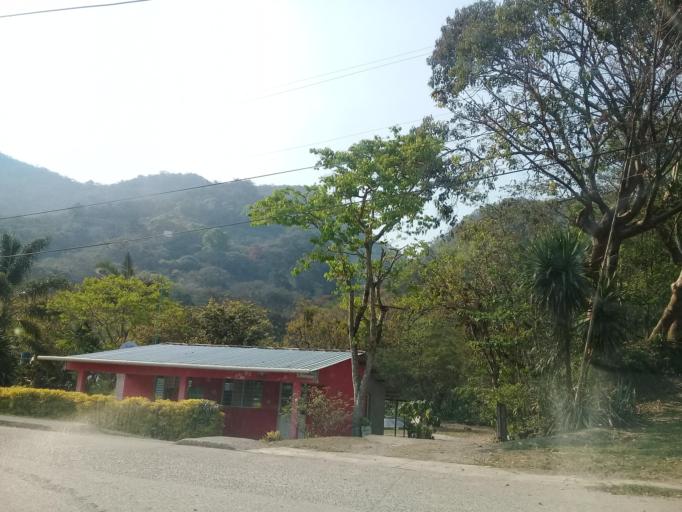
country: MX
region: Veracruz
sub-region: Ixtaczoquitlan
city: Campo Chico
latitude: 18.8374
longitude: -97.0316
